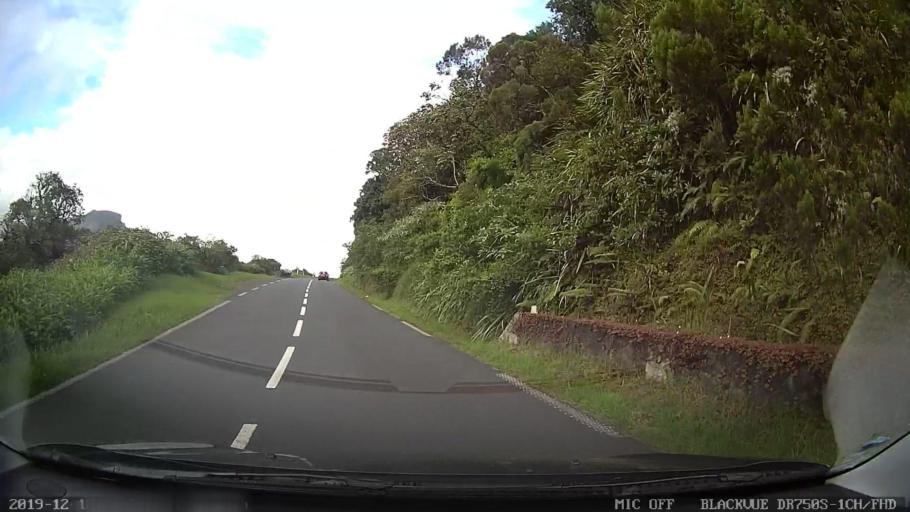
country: RE
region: Reunion
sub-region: Reunion
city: Cilaos
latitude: -21.1627
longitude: 55.5961
